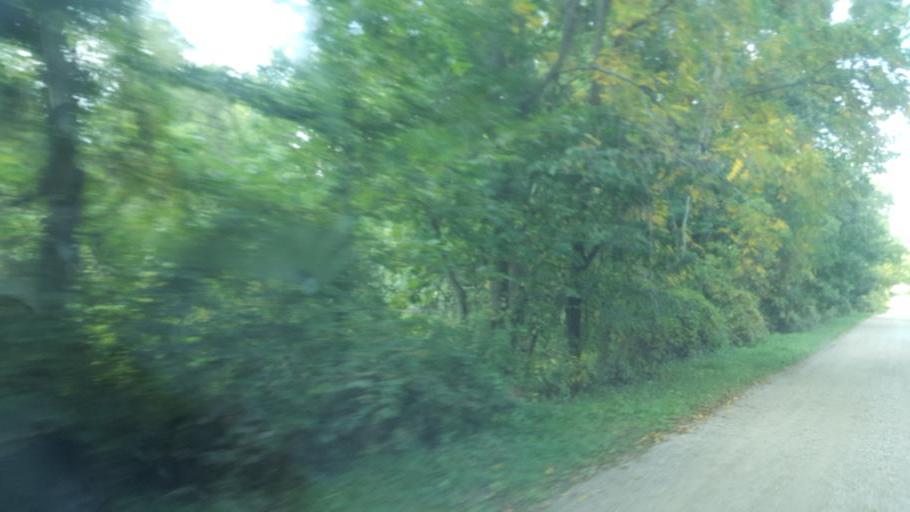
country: US
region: Ohio
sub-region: Knox County
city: Centerburg
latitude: 40.3949
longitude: -82.6307
